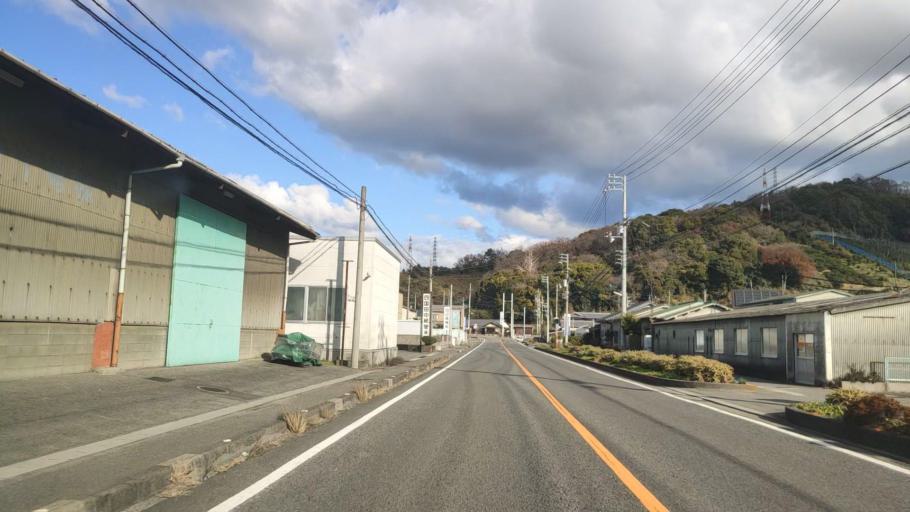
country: JP
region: Ehime
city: Masaki-cho
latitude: 33.8386
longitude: 132.7092
